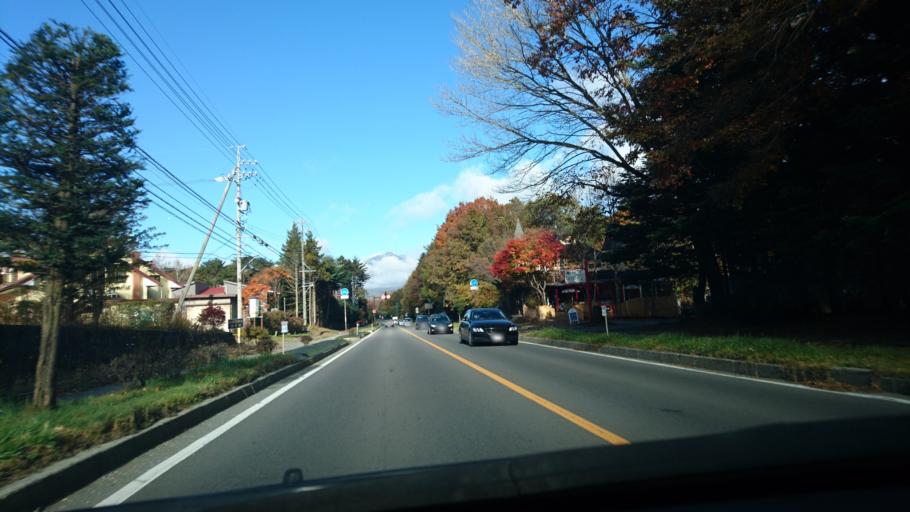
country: JP
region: Nagano
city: Saku
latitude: 36.3281
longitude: 138.6141
